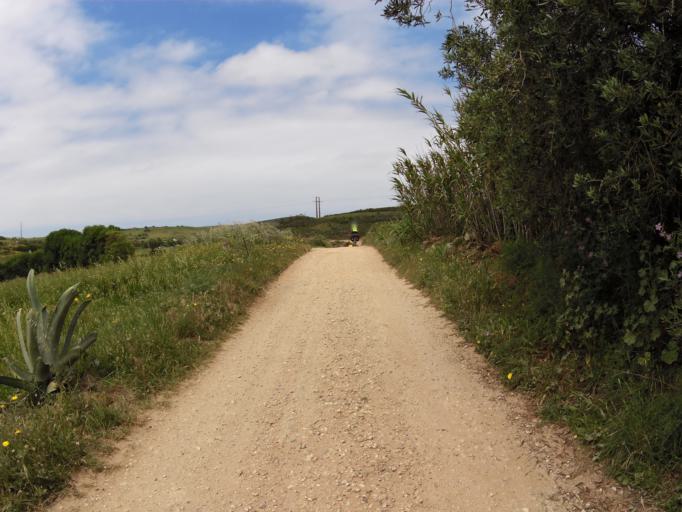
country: PT
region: Faro
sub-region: Vila do Bispo
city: Vila do Bispo
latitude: 37.0854
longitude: -8.8928
